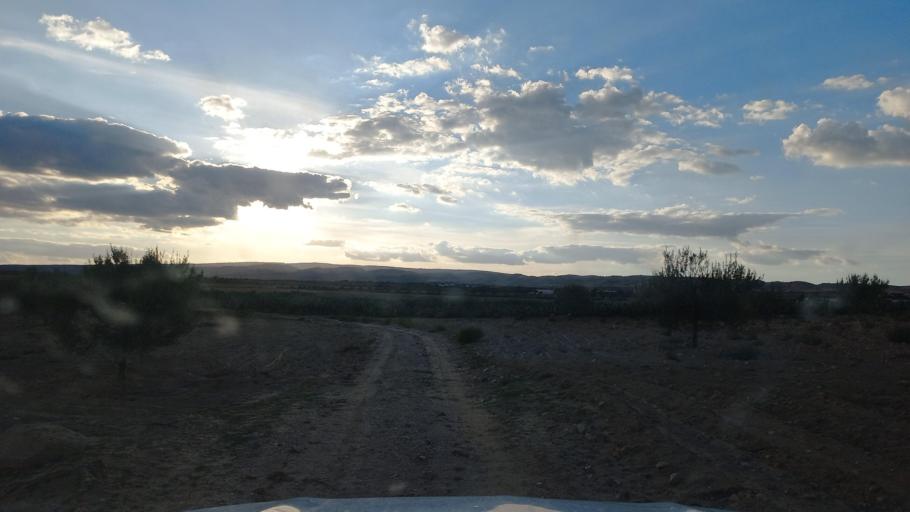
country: TN
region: Al Qasrayn
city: Sbiba
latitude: 35.3530
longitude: 9.0284
